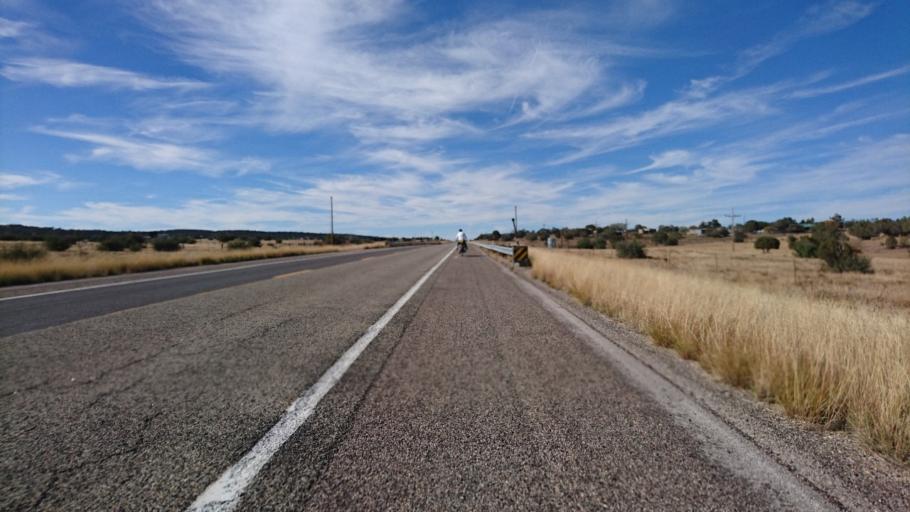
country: US
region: Arizona
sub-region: Mohave County
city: Peach Springs
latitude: 35.4979
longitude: -113.1683
